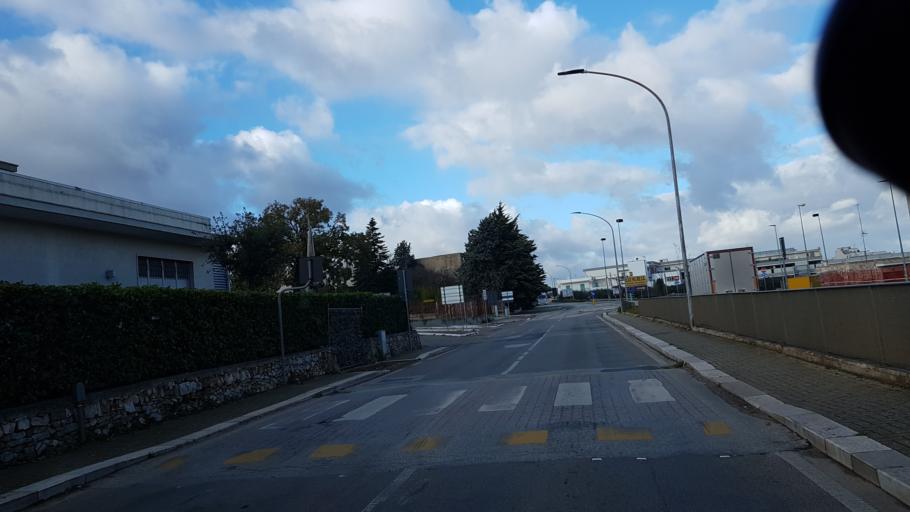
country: IT
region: Apulia
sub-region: Provincia di Bari
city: Alberobello
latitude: 40.7874
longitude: 17.2442
